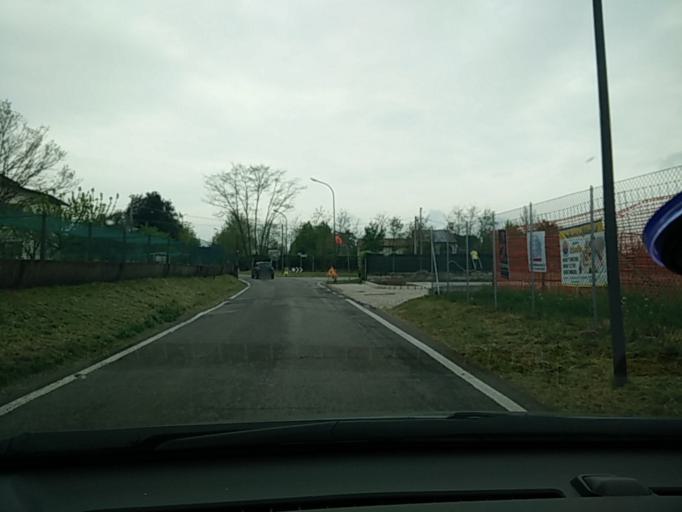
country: IT
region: Veneto
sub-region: Provincia di Treviso
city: Ponzano
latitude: 45.6977
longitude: 12.2226
